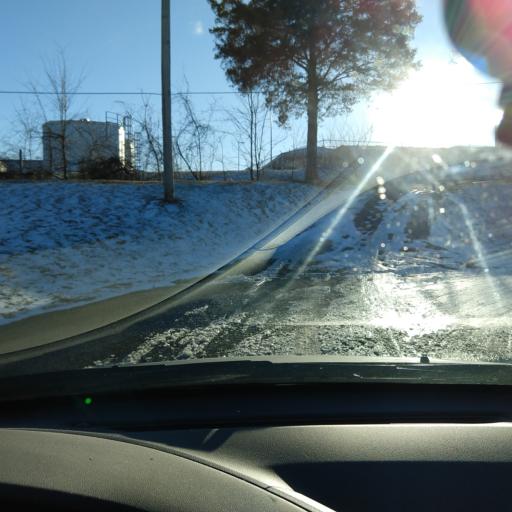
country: US
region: Virginia
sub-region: City of Bedford
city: Bedford
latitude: 37.3380
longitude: -79.5537
